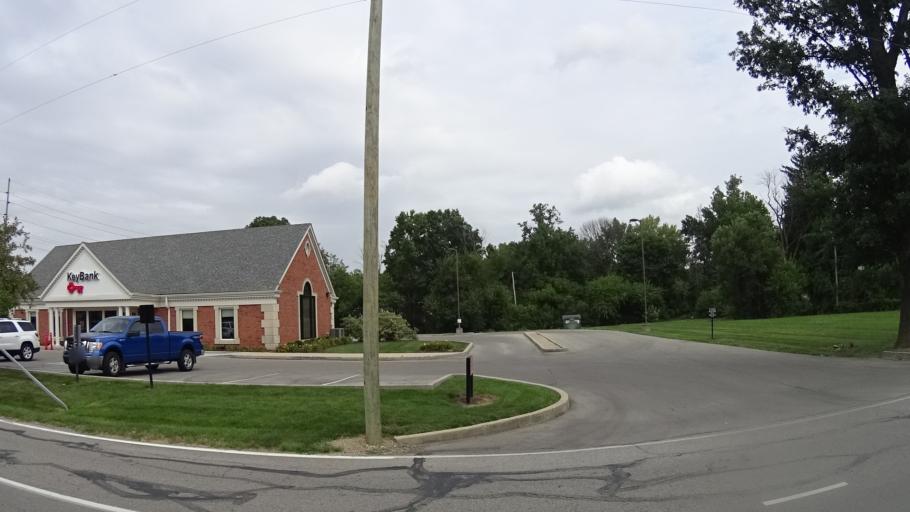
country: US
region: Indiana
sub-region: Madison County
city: Edgewood
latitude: 40.1015
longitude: -85.7294
